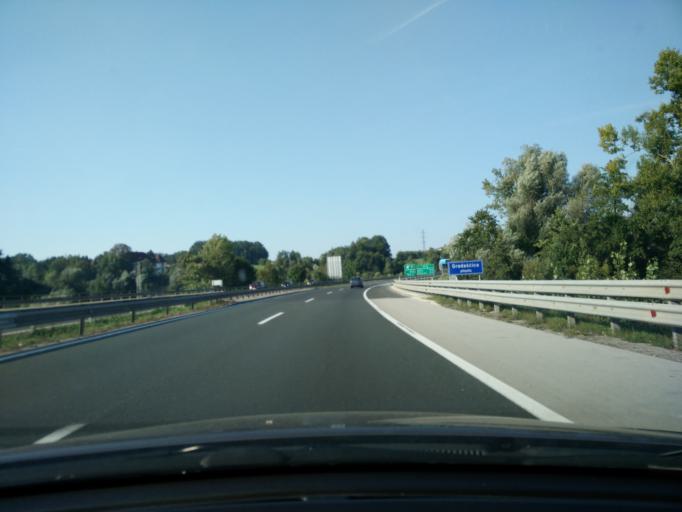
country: SI
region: Brezovica
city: Vnanje Gorice
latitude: 46.0444
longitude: 14.4467
